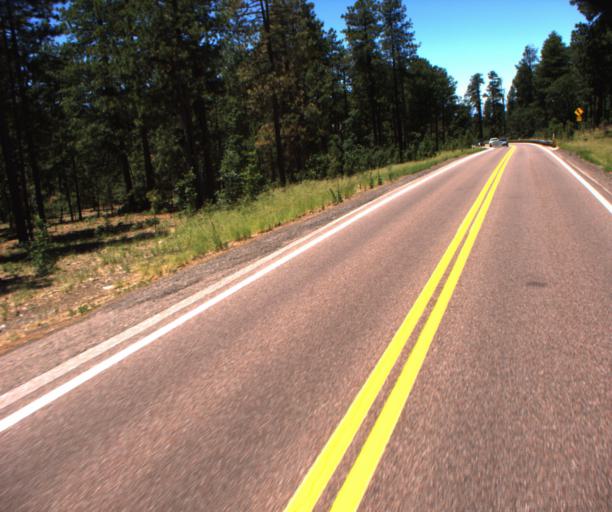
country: US
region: Arizona
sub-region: Gila County
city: Pine
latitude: 34.4430
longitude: -111.4609
